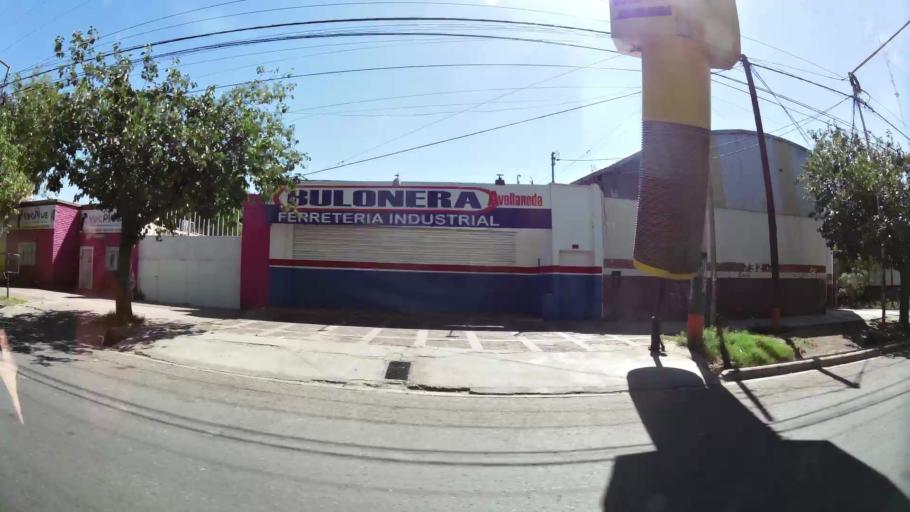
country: AR
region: Mendoza
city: Villa Nueva
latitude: -32.8920
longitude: -68.7888
